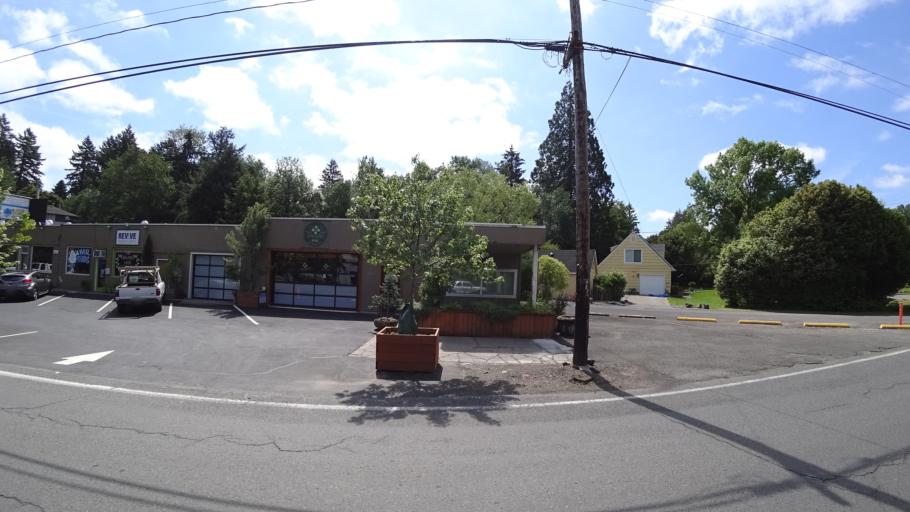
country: US
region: Oregon
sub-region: Washington County
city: Garden Home-Whitford
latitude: 45.4656
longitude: -122.7228
